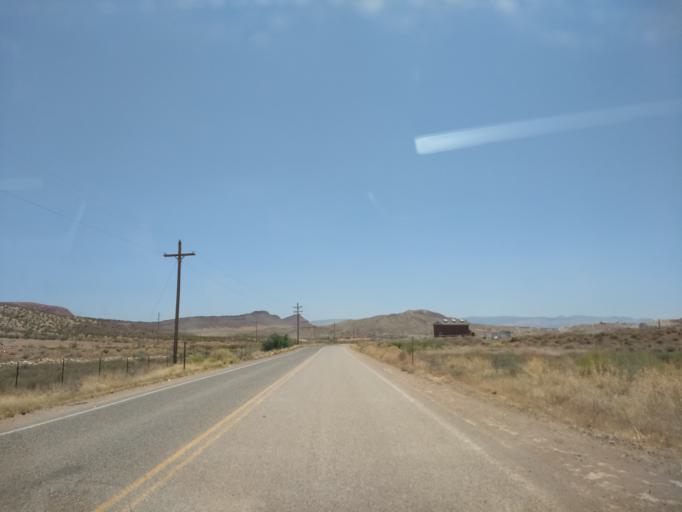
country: US
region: Utah
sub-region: Washington County
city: Washington
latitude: 37.1356
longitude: -113.4510
